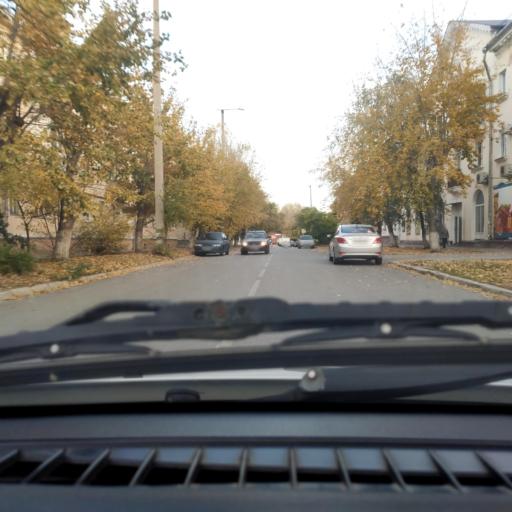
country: RU
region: Samara
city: Zhigulevsk
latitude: 53.4650
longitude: 49.5330
